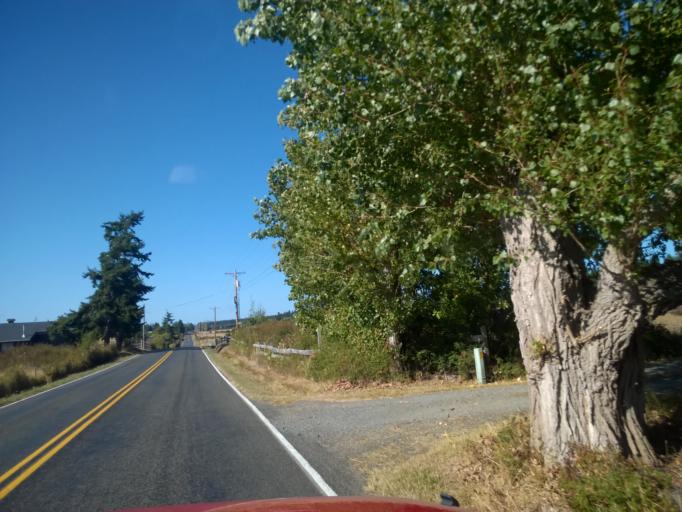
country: US
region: Washington
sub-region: San Juan County
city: Friday Harbor
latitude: 48.4798
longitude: -122.8990
